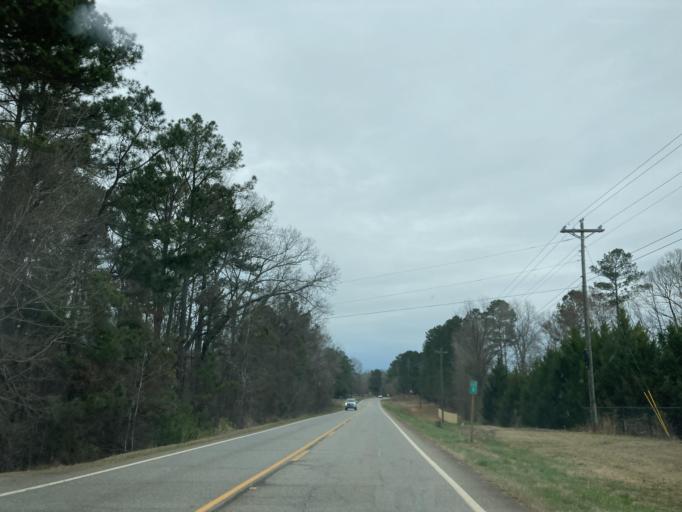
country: US
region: Georgia
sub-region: Jones County
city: Gray
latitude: 32.9817
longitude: -83.6073
